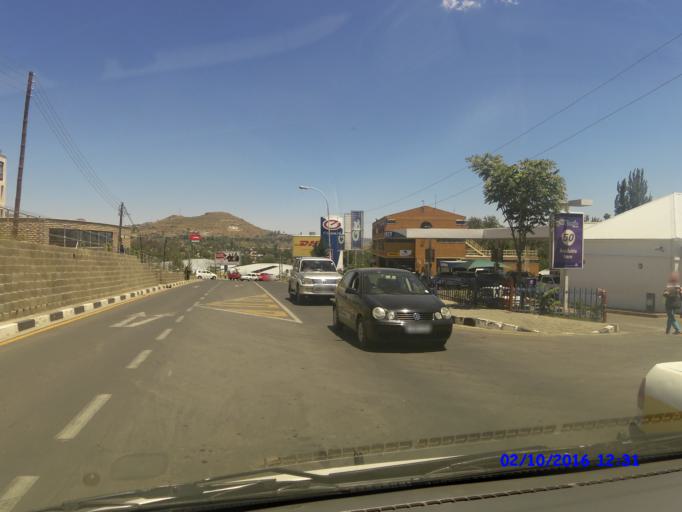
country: LS
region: Maseru
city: Maseru
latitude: -29.3146
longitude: 27.4799
